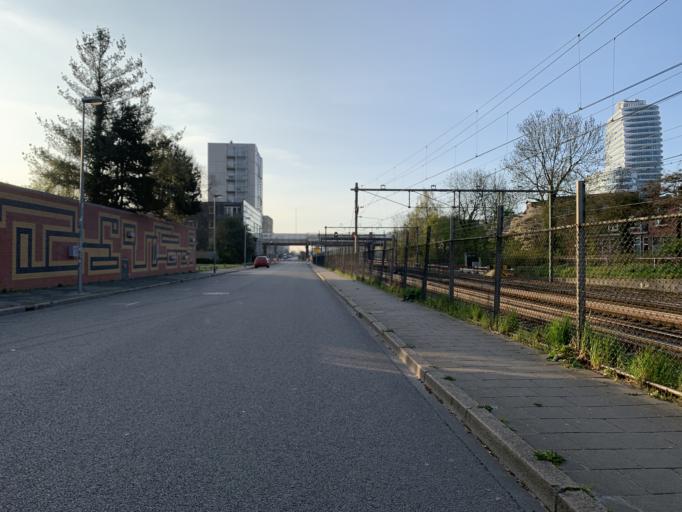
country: NL
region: Groningen
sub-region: Gemeente Groningen
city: Groningen
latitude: 53.2088
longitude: 6.5776
